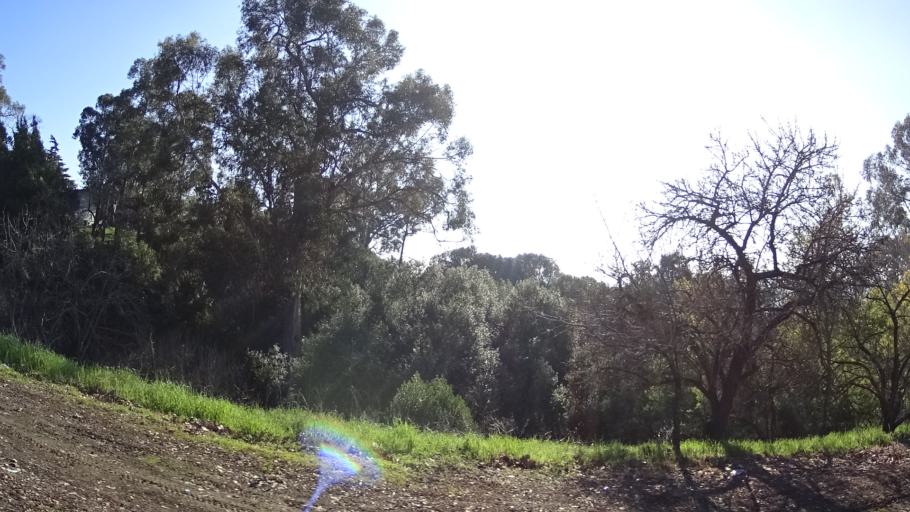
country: US
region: California
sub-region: Alameda County
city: Hayward
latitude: 37.6603
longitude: -122.0675
